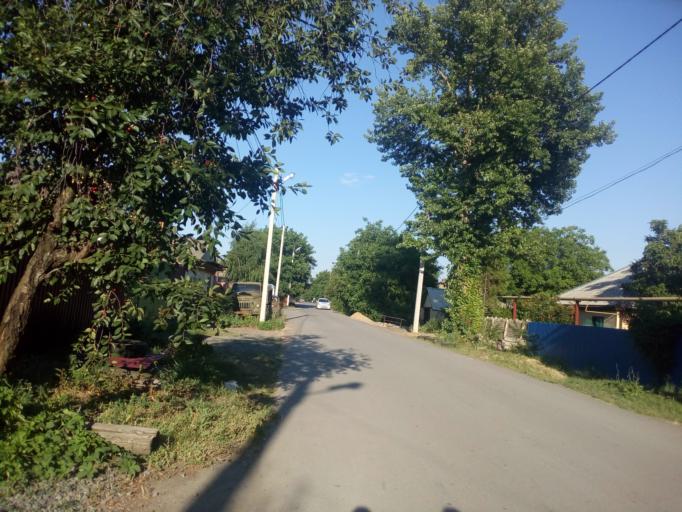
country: RU
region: Rostov
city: Sholokhovskiy
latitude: 48.2772
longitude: 41.0468
